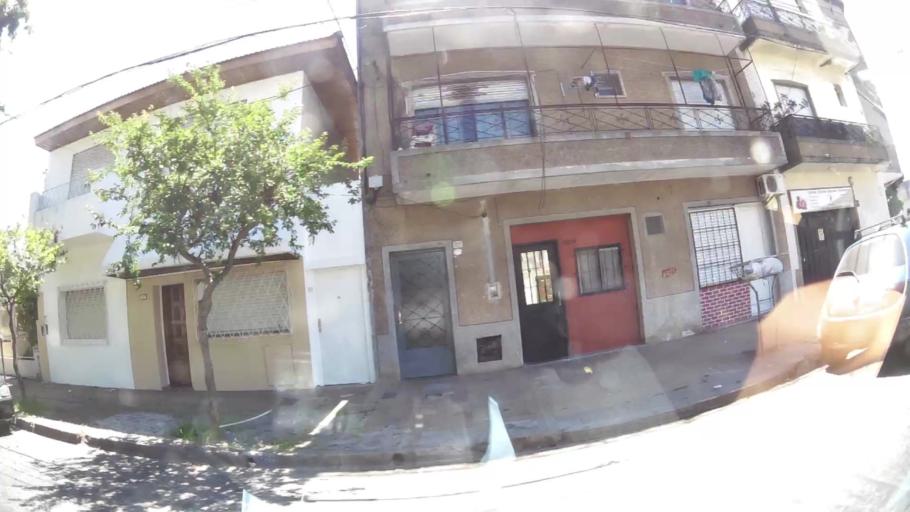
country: AR
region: Buenos Aires
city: Caseros
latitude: -34.5906
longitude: -58.5593
